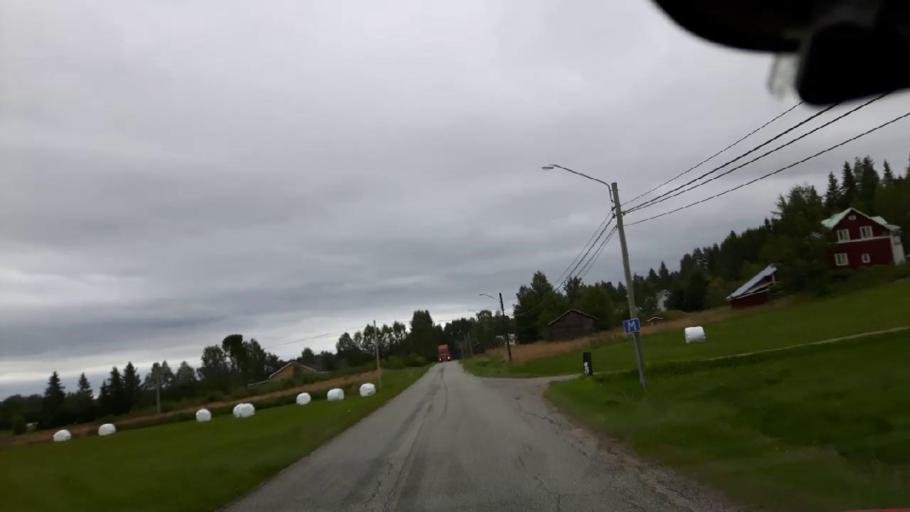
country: SE
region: Vaesternorrland
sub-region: Ange Kommun
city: Fransta
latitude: 62.7719
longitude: 15.9997
